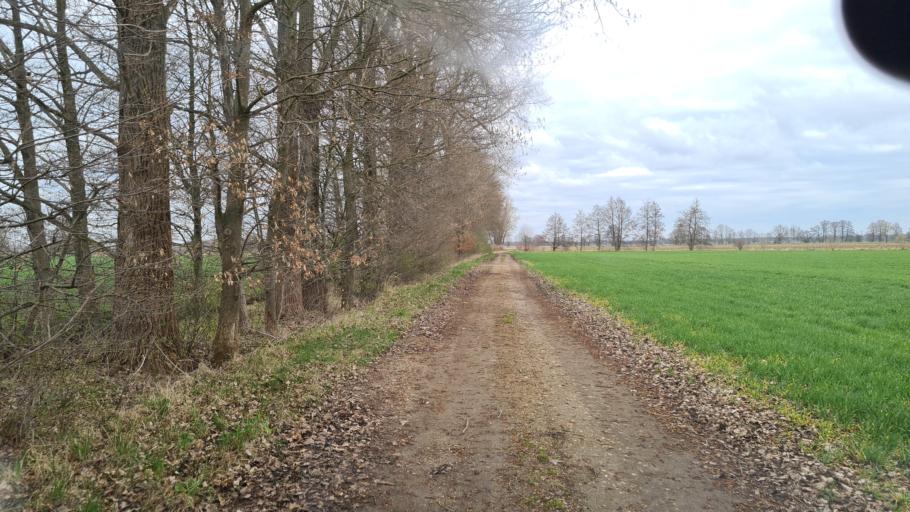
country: DE
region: Brandenburg
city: Schonewalde
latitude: 51.6637
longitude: 13.5767
